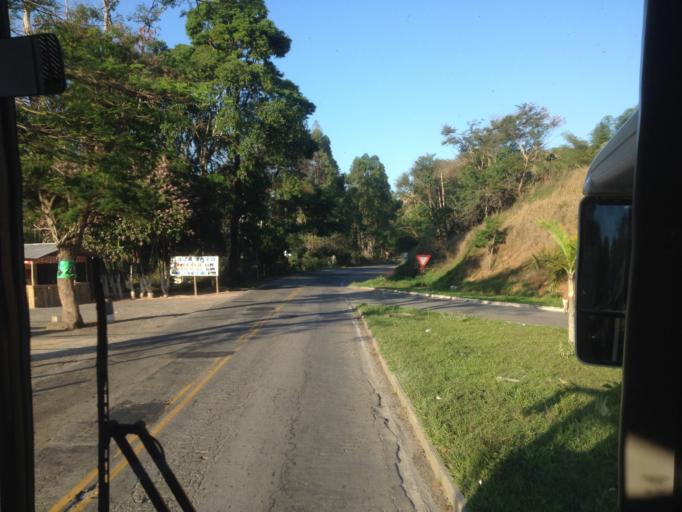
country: BR
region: Minas Gerais
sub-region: Juiz De Fora
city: Juiz de Fora
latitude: -21.6778
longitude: -43.3442
